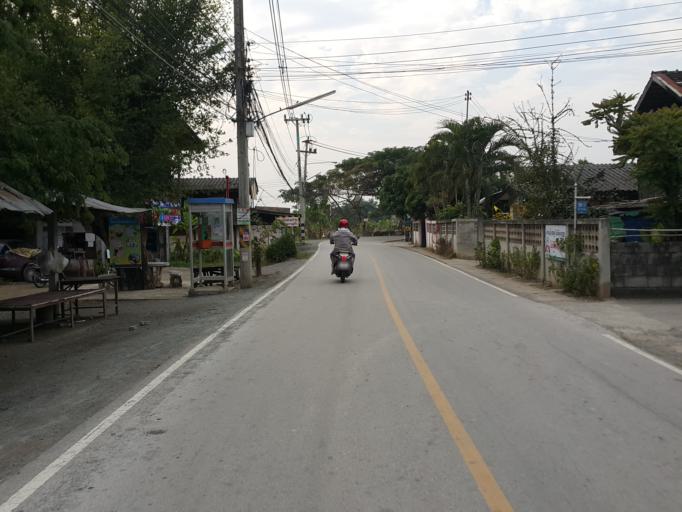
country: TH
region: Chiang Mai
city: San Kamphaeng
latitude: 18.8353
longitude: 99.1533
